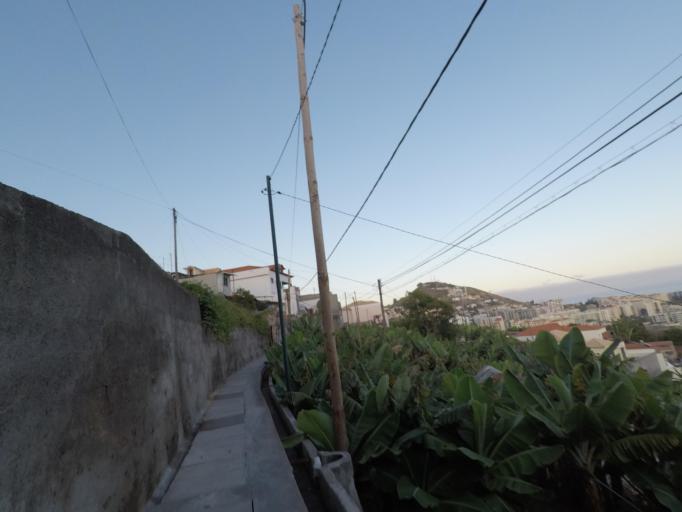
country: PT
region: Madeira
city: Camara de Lobos
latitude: 32.6449
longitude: -16.9539
